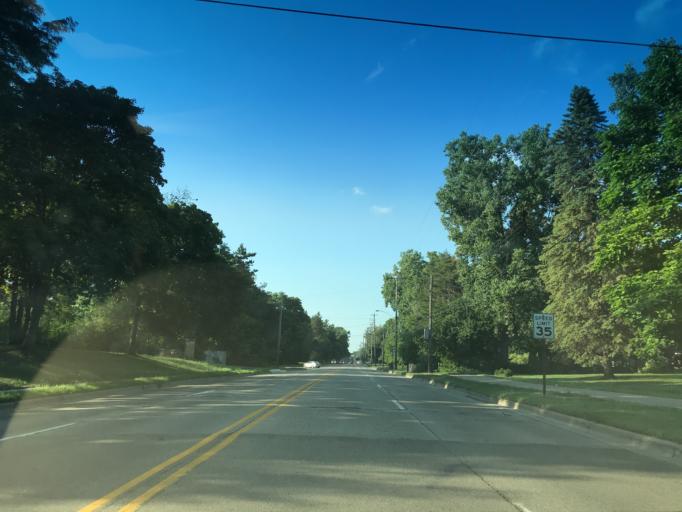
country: US
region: Michigan
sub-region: Eaton County
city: Waverly
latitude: 42.6987
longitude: -84.6031
